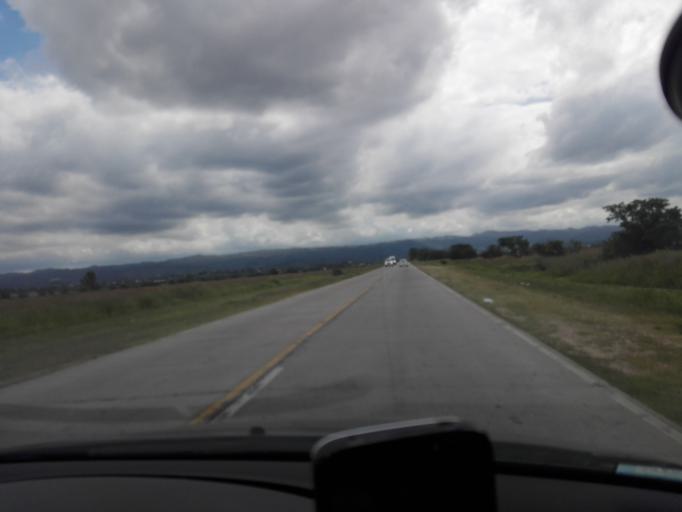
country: AR
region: Cordoba
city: Alta Gracia
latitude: -31.6348
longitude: -64.4113
